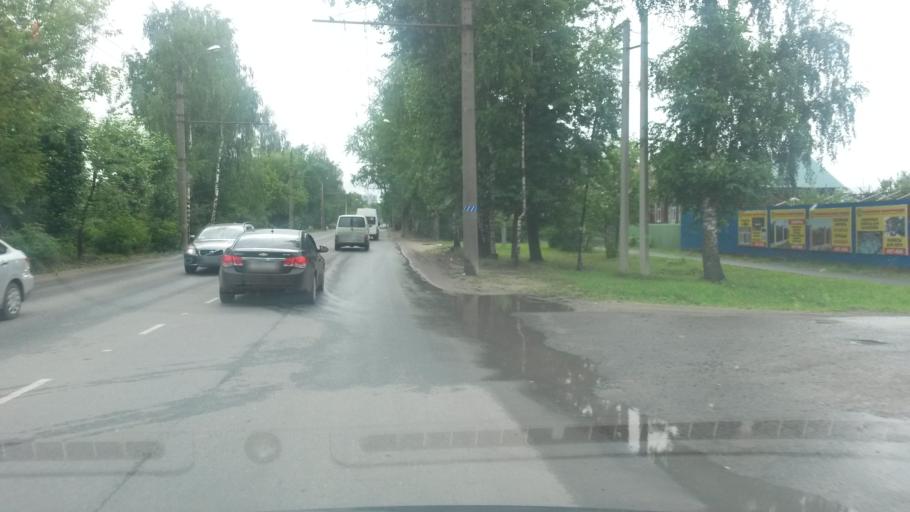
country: RU
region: Ivanovo
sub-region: Gorod Ivanovo
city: Ivanovo
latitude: 57.0149
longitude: 40.9310
